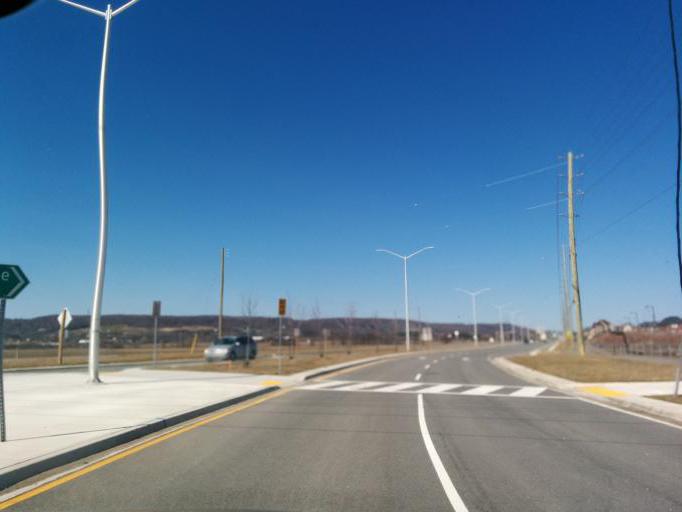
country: CA
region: Ontario
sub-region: Halton
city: Milton
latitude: 43.4766
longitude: -79.8702
